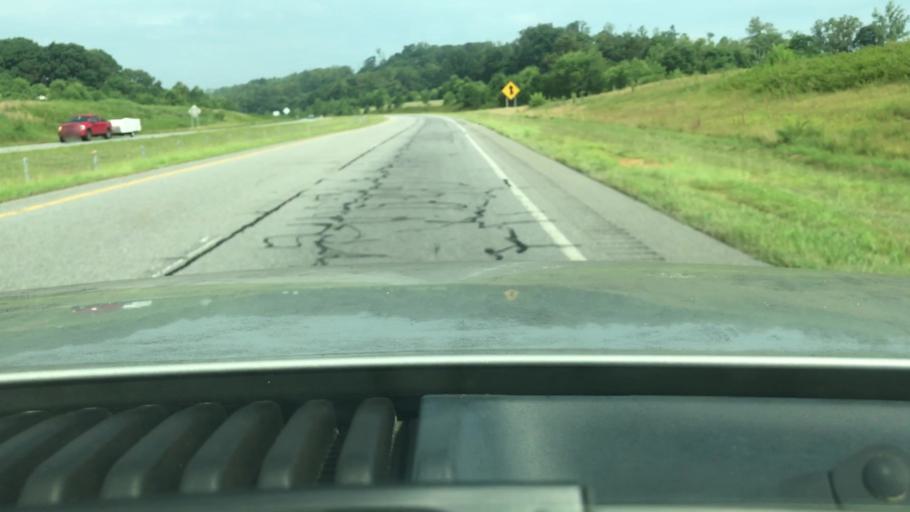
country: US
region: North Carolina
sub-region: Yadkin County
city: Jonesville
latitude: 36.1437
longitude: -80.8963
